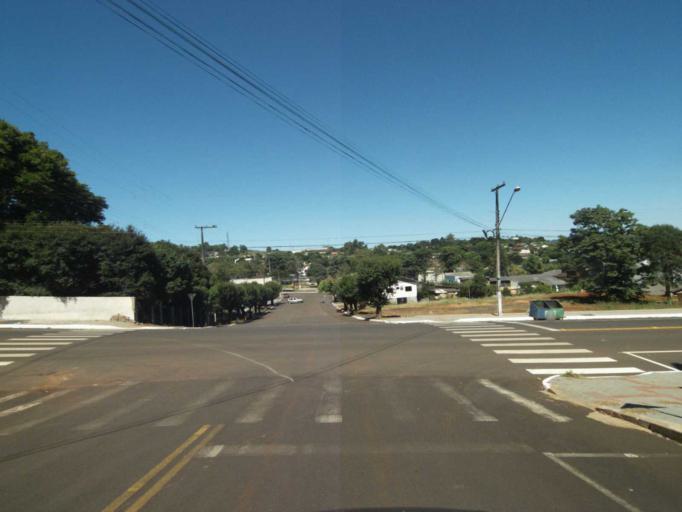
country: BR
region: Parana
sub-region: Coronel Vivida
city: Coronel Vivida
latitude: -25.9608
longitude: -52.8168
